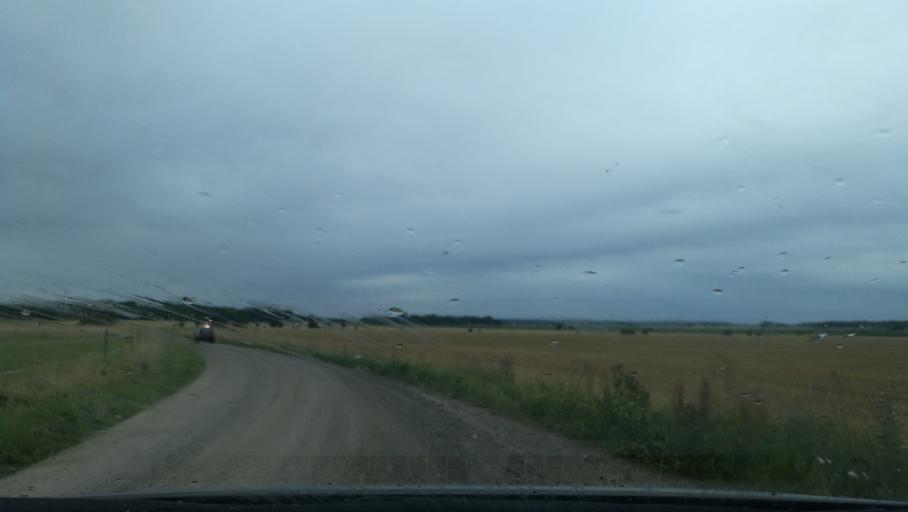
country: SE
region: Vaestmanland
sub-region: Vasteras
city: Tillberga
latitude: 59.7169
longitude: 16.6265
